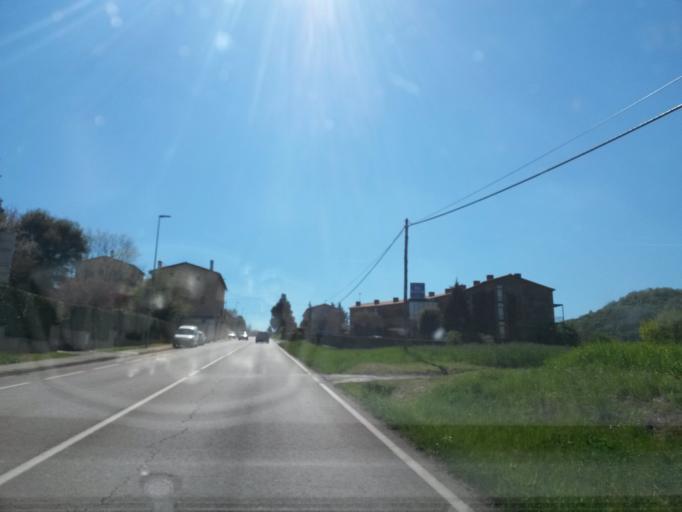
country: ES
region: Catalonia
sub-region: Provincia de Girona
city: Olot
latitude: 42.1749
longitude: 2.4931
